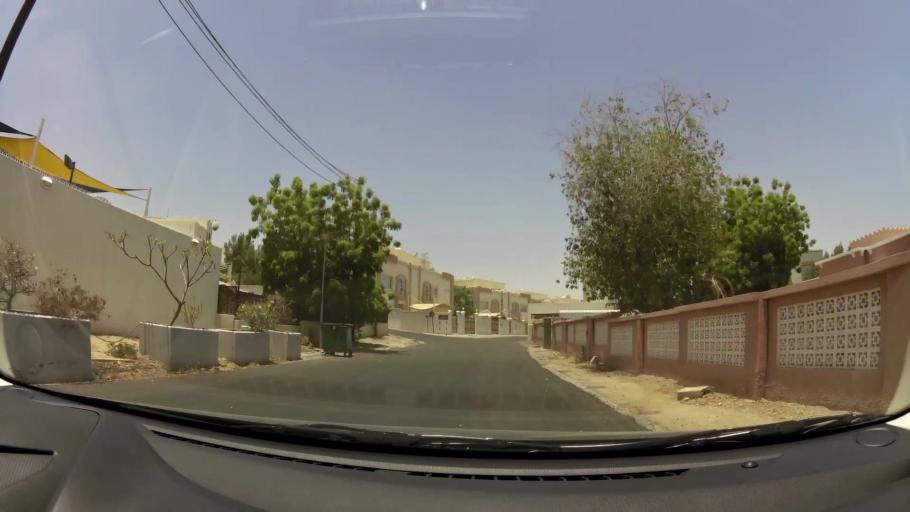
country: OM
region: Muhafazat Masqat
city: Bawshar
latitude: 23.6051
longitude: 58.4558
